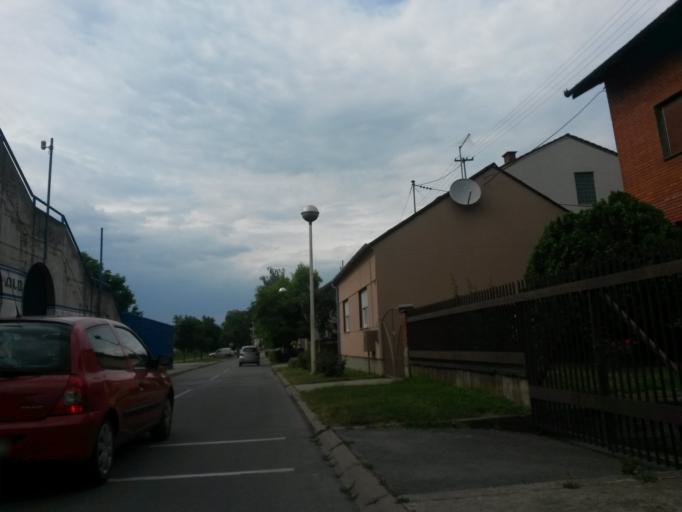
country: HR
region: Osjecko-Baranjska
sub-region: Grad Osijek
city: Osijek
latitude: 45.5456
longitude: 18.6964
